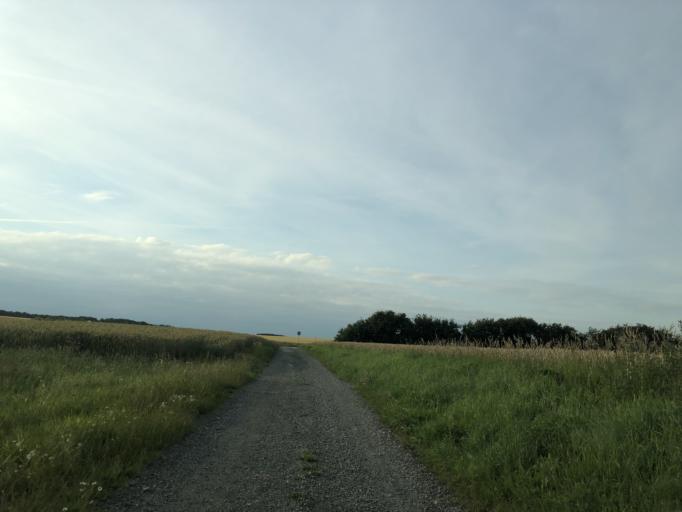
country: DK
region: South Denmark
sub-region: Fredericia Kommune
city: Taulov
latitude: 55.5915
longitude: 9.6157
